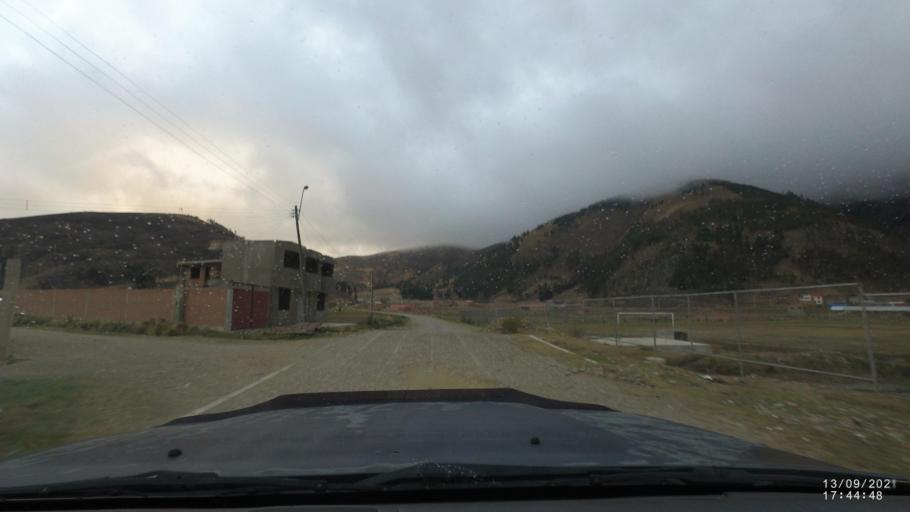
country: BO
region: Cochabamba
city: Colomi
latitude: -17.3738
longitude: -65.8306
